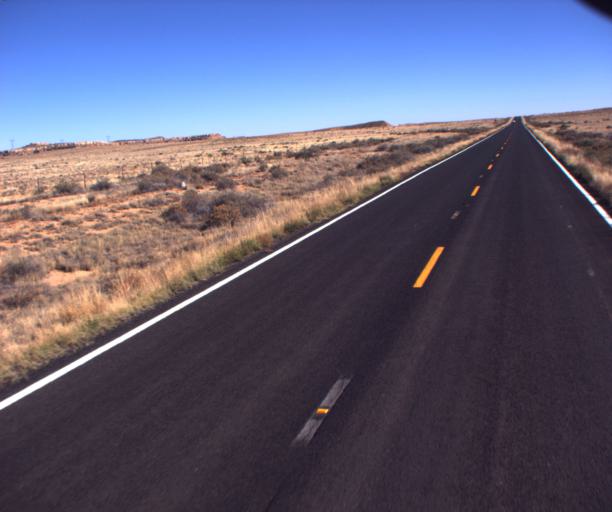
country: US
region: Arizona
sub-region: Navajo County
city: First Mesa
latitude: 35.9743
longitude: -110.7697
